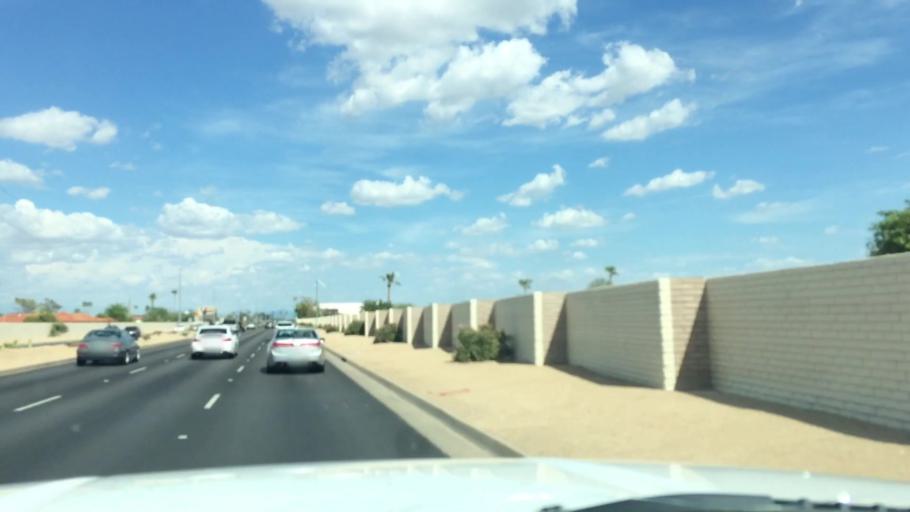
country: US
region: Arizona
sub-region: Maricopa County
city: Sun City
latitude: 33.6384
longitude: -112.2678
